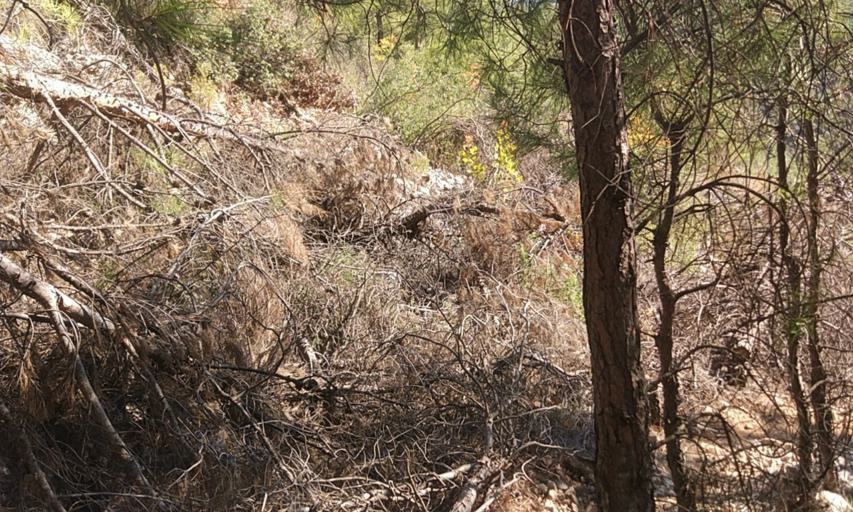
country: TR
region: Antalya
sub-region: Kemer
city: Goeynuek
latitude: 36.6334
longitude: 30.4473
